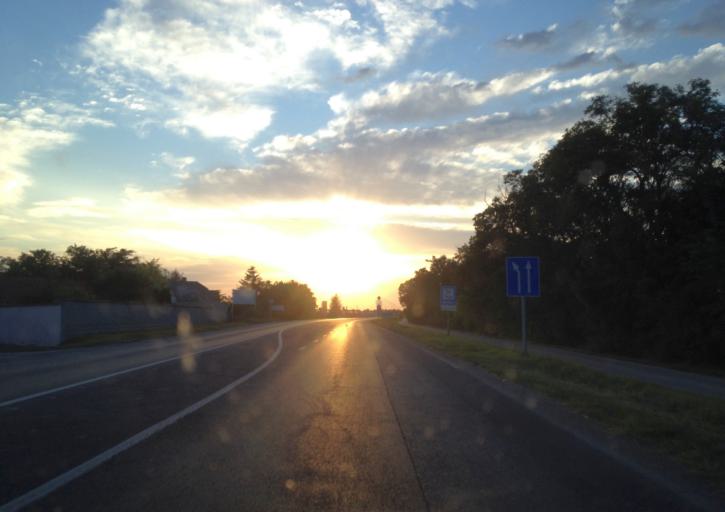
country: HU
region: Gyor-Moson-Sopron
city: Mosonmagyarovar
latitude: 47.8989
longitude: 17.2047
